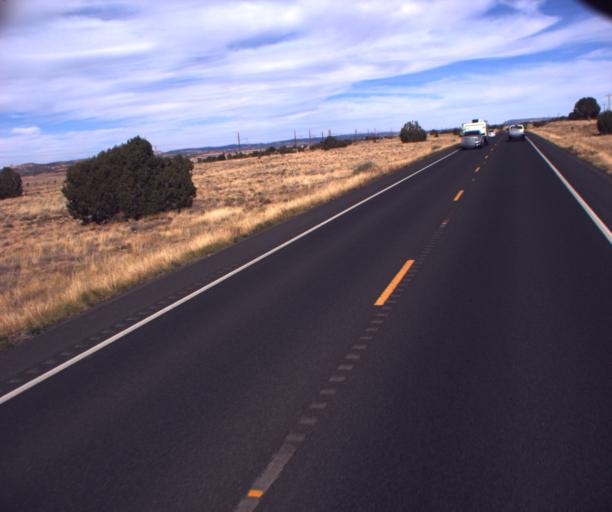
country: US
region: Arizona
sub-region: Navajo County
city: Kayenta
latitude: 36.4901
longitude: -110.6334
